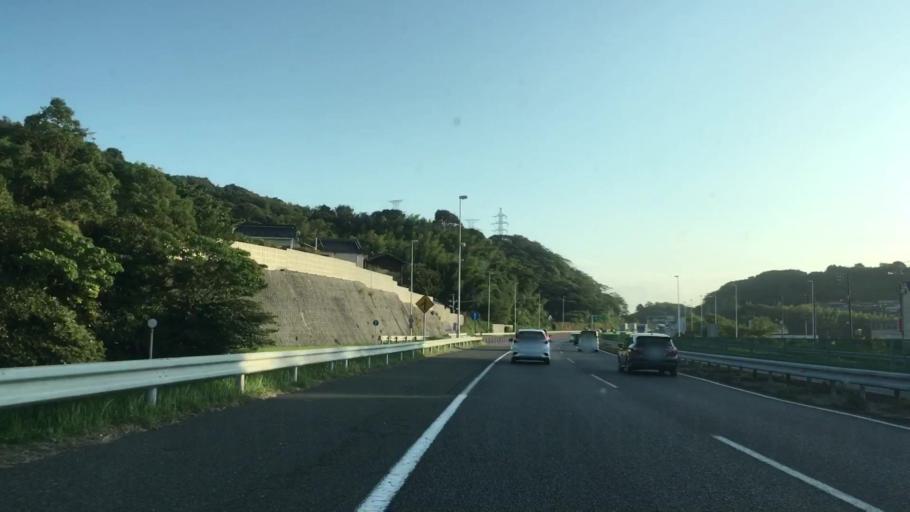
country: JP
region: Yamaguchi
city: Shimonoseki
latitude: 33.9774
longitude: 130.9524
